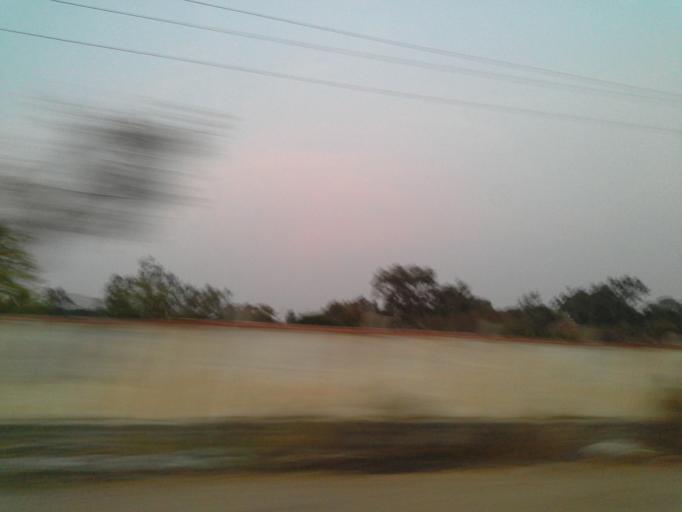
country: IN
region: Telangana
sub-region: Hyderabad
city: Hyderabad
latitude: 17.3232
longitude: 78.3788
